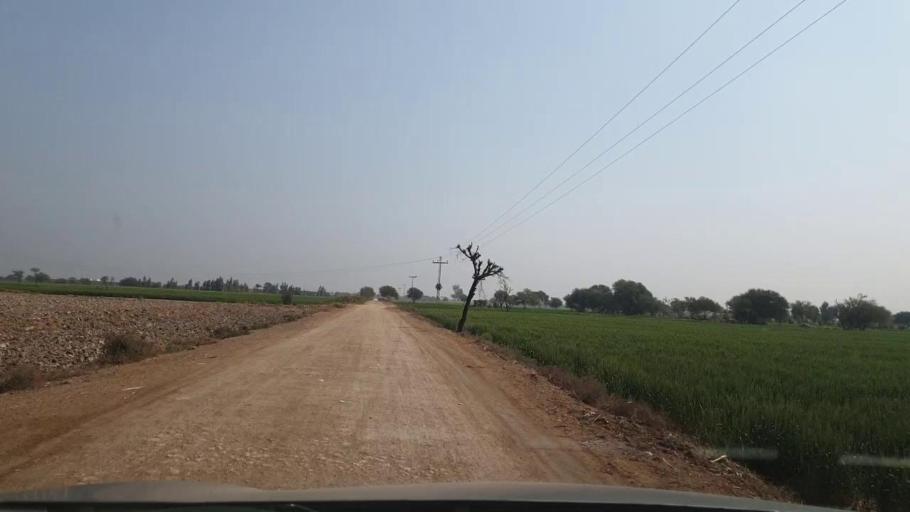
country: PK
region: Sindh
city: Tando Allahyar
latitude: 25.5375
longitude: 68.7970
